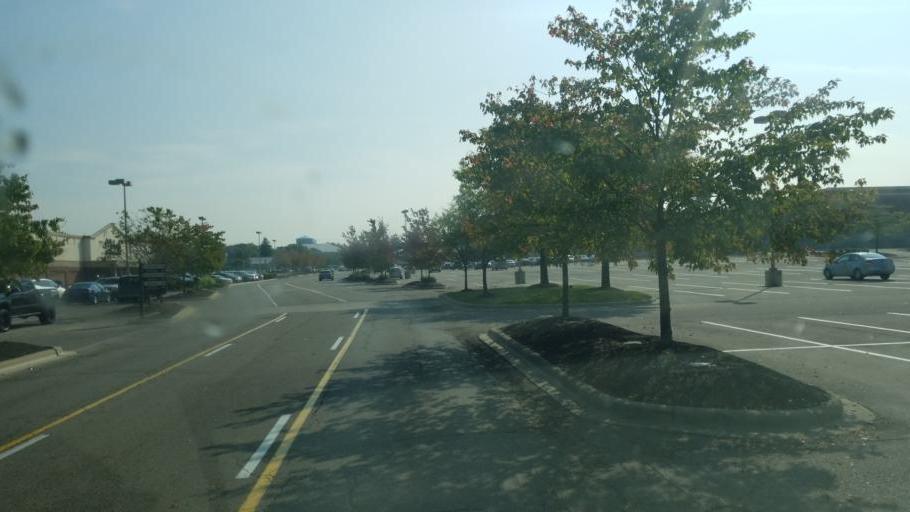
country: US
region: Ohio
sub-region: Franklin County
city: Worthington
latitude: 40.0659
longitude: -83.0231
